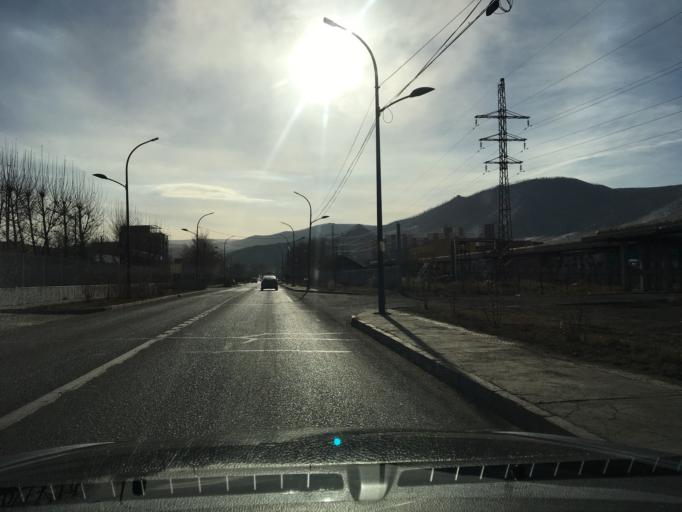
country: MN
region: Ulaanbaatar
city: Ulaanbaatar
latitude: 47.8965
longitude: 106.8717
